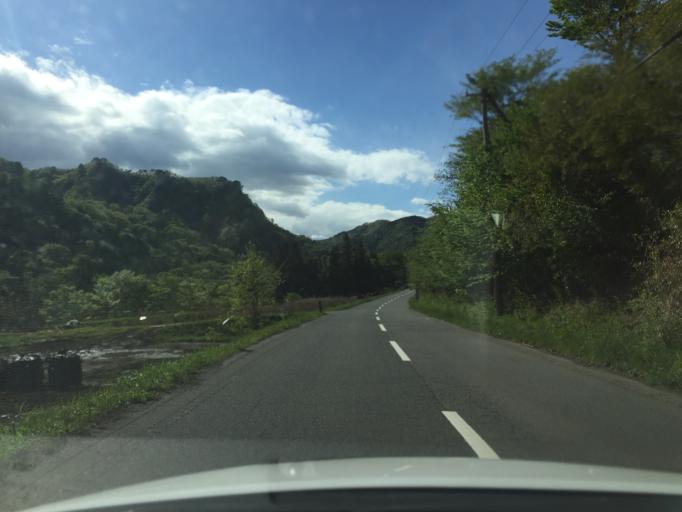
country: JP
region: Miyagi
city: Marumori
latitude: 37.7376
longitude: 140.8080
